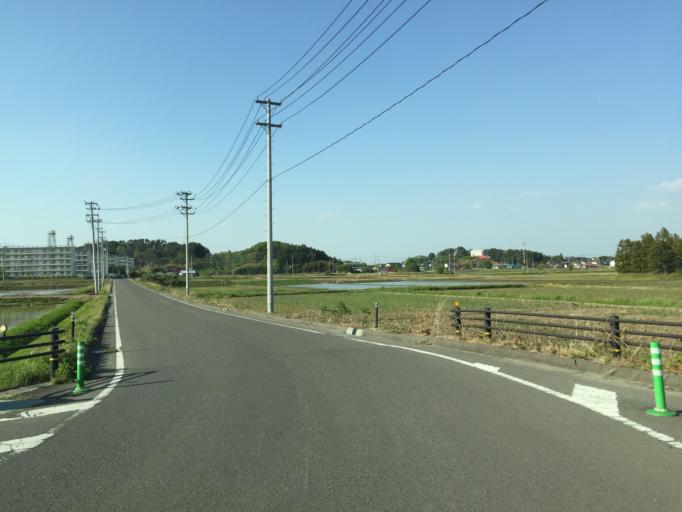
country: JP
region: Fukushima
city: Koriyama
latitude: 37.4017
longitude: 140.3213
